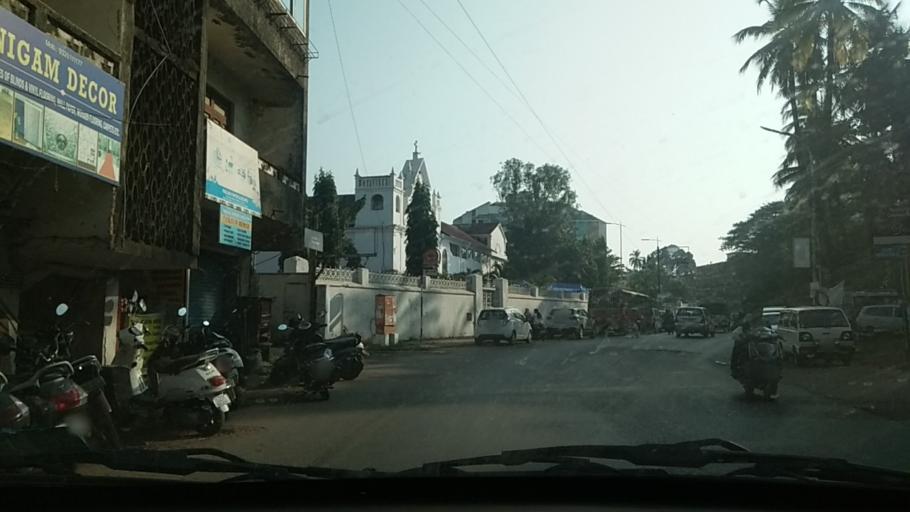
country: IN
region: Goa
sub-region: North Goa
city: Panaji
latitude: 15.4920
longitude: 73.8204
